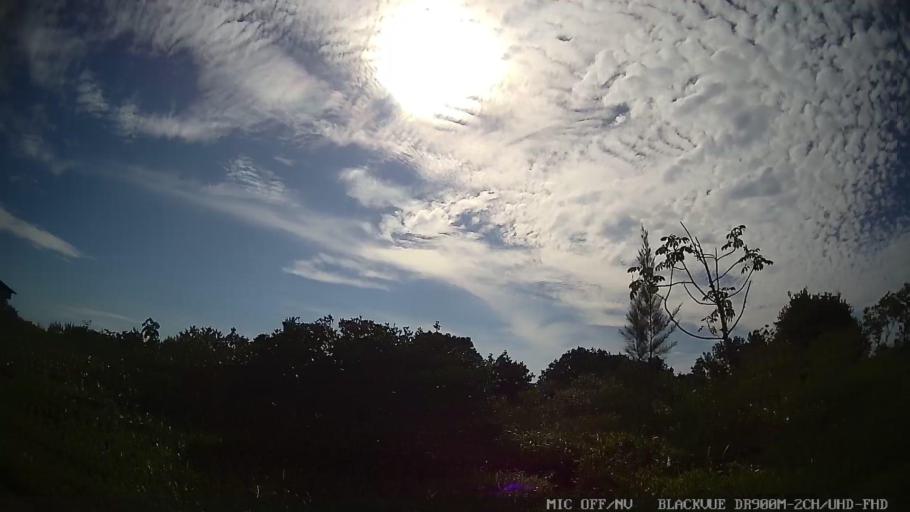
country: BR
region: Sao Paulo
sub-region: Iguape
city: Iguape
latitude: -24.7685
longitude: -47.5913
